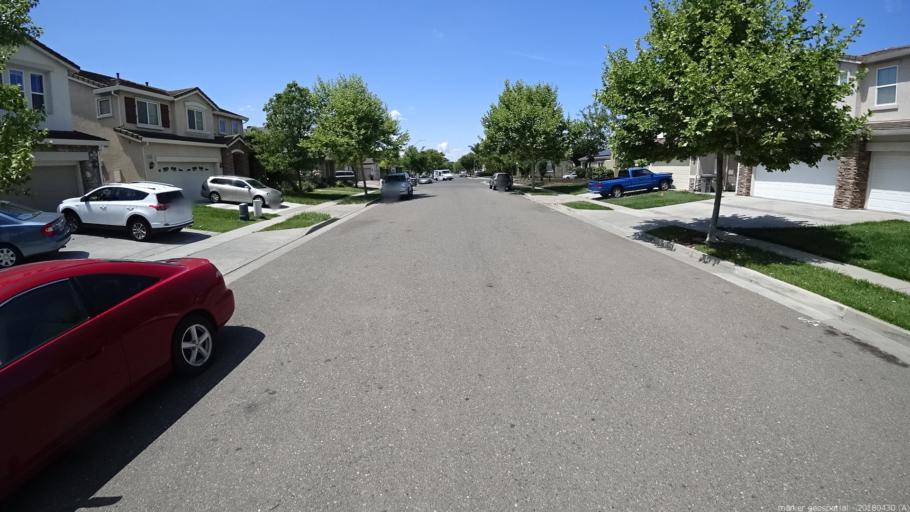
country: US
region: California
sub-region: Yolo County
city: West Sacramento
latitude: 38.5459
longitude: -121.5279
